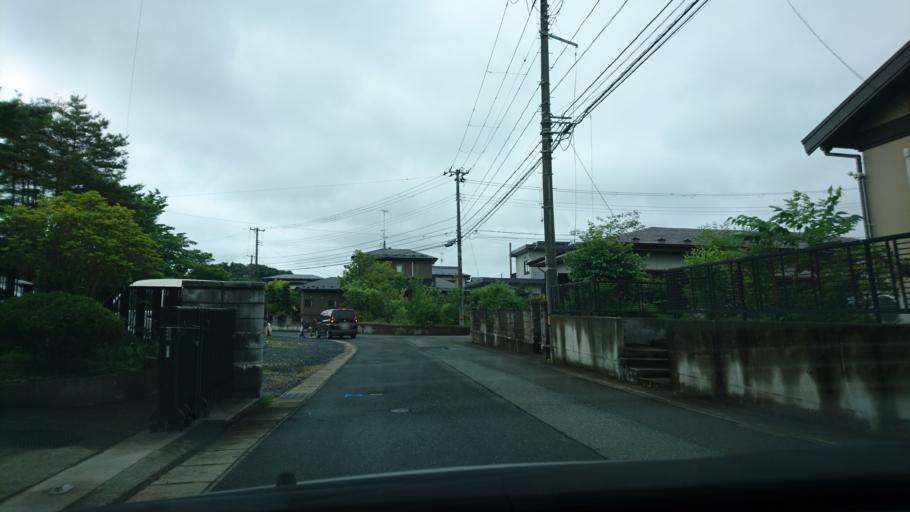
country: JP
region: Iwate
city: Ichinoseki
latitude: 38.9103
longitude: 141.1388
